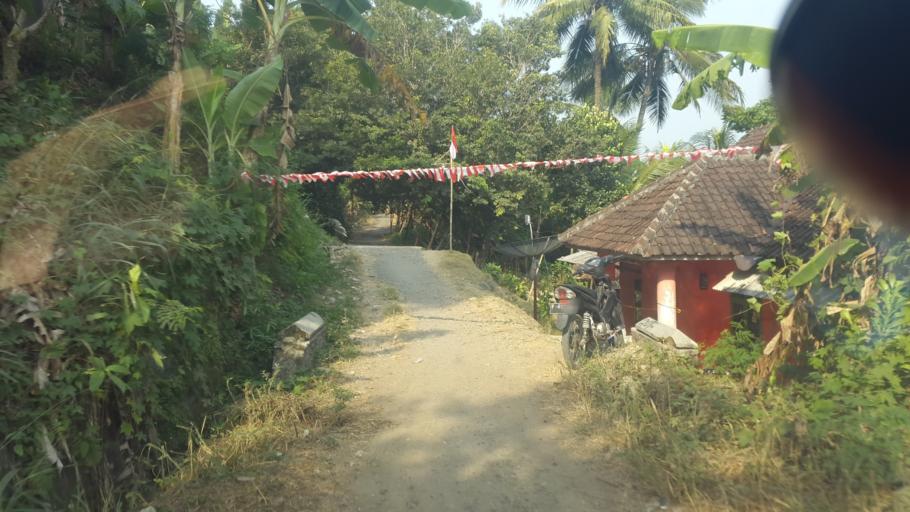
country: ID
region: West Java
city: Bojonggaling
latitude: -7.0132
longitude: 106.6424
